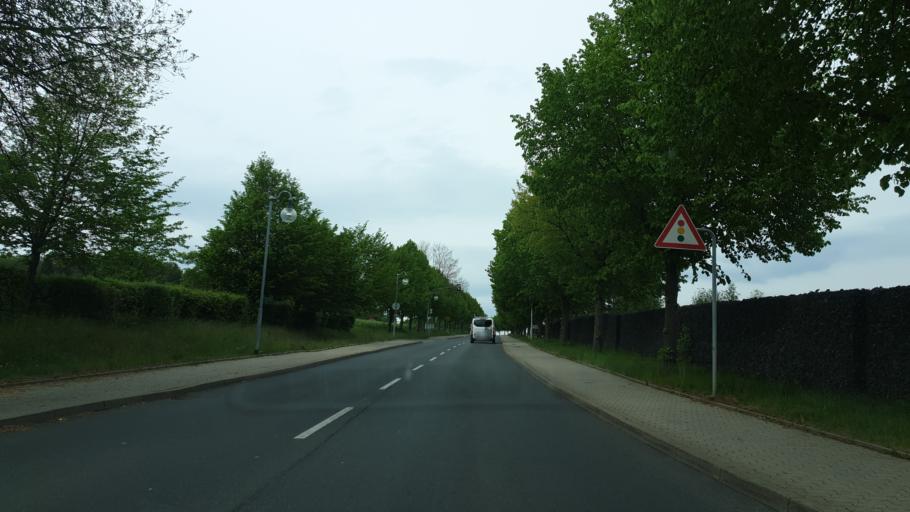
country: DE
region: Saxony
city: Dippoldiswalde
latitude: 50.9068
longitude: 13.6739
